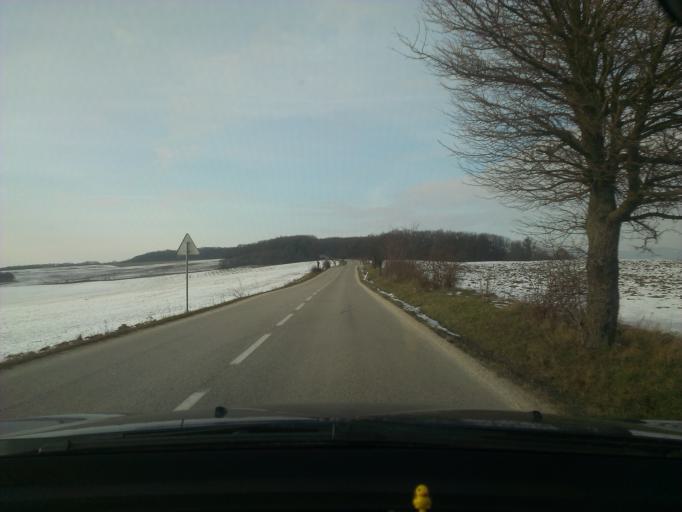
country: SK
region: Nitriansky
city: Stara Tura
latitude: 48.7172
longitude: 17.6855
